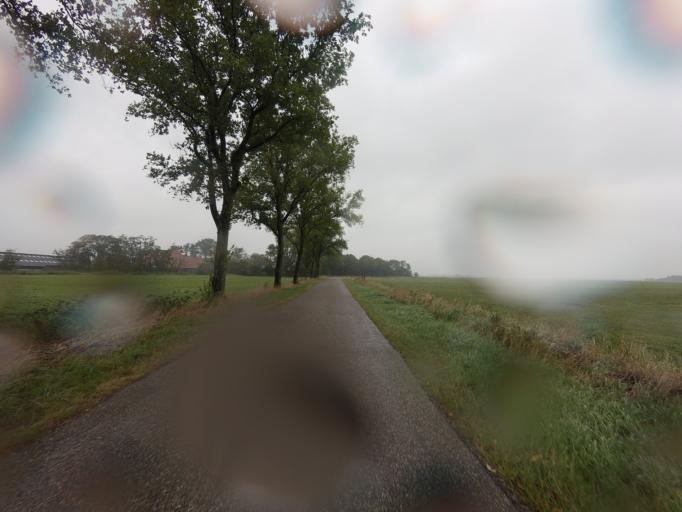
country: NL
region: Friesland
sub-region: Gemeente Boarnsterhim
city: Aldeboarn
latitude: 53.0727
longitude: 5.9286
